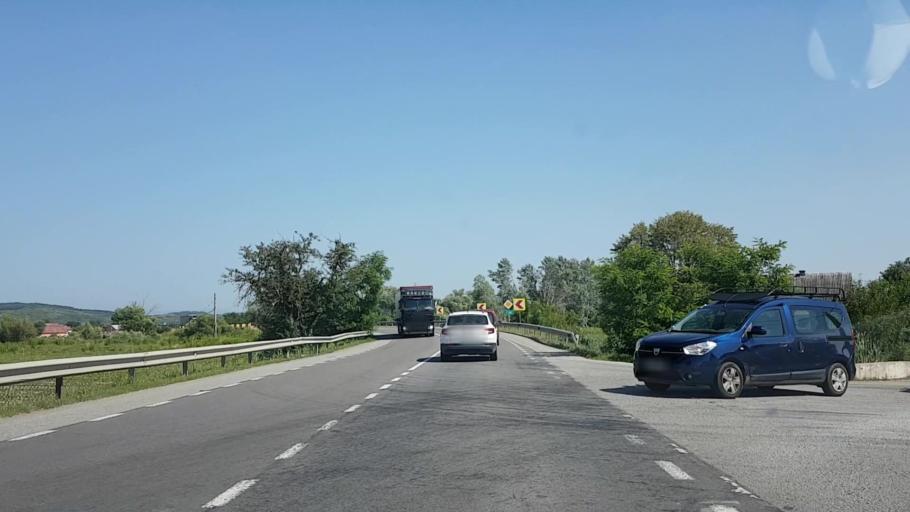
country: RO
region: Bistrita-Nasaud
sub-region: Comuna Sintereag
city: Sintereag
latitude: 47.1804
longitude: 24.2699
